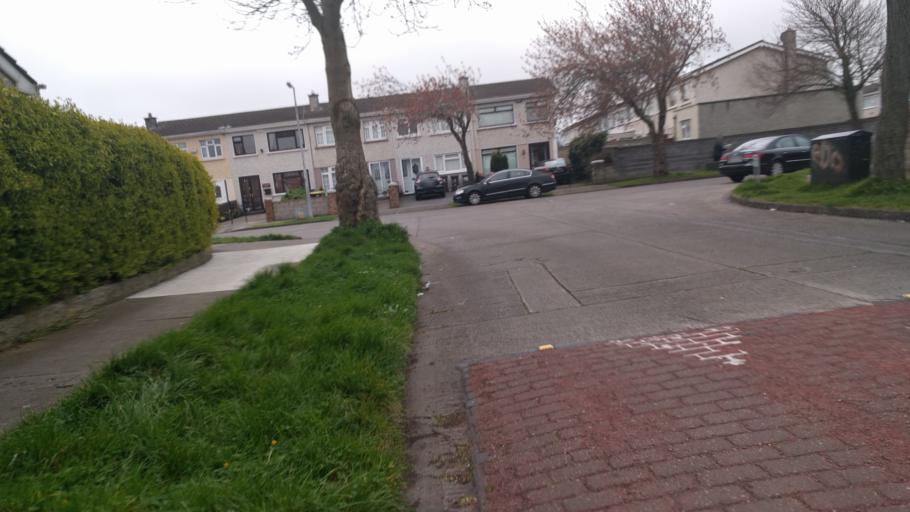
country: IE
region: Leinster
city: Tallaght
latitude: 53.2877
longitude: -6.3850
